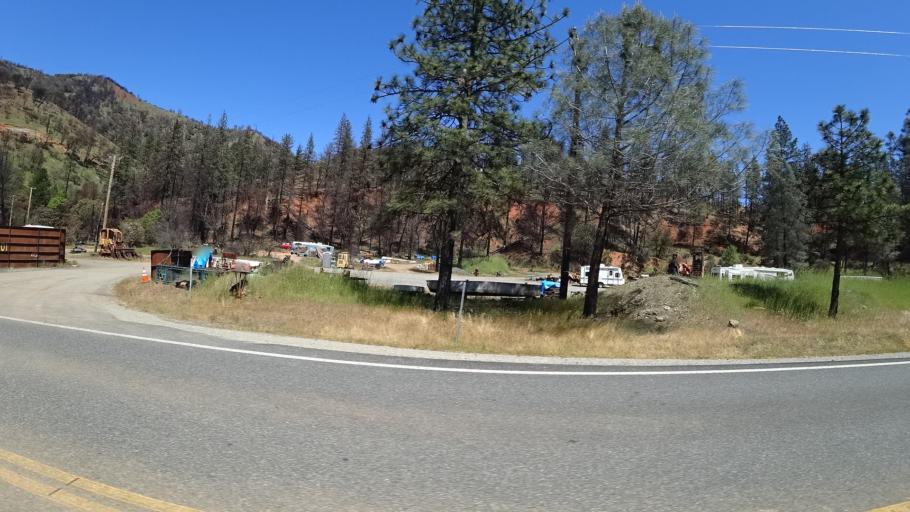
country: US
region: California
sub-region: Trinity County
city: Weaverville
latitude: 40.7647
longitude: -123.1013
